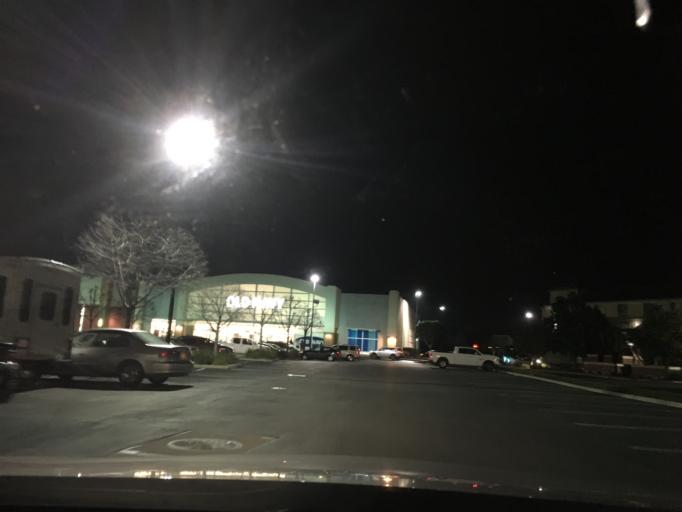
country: US
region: California
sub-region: Sacramento County
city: Laguna
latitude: 38.4245
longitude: -121.3996
